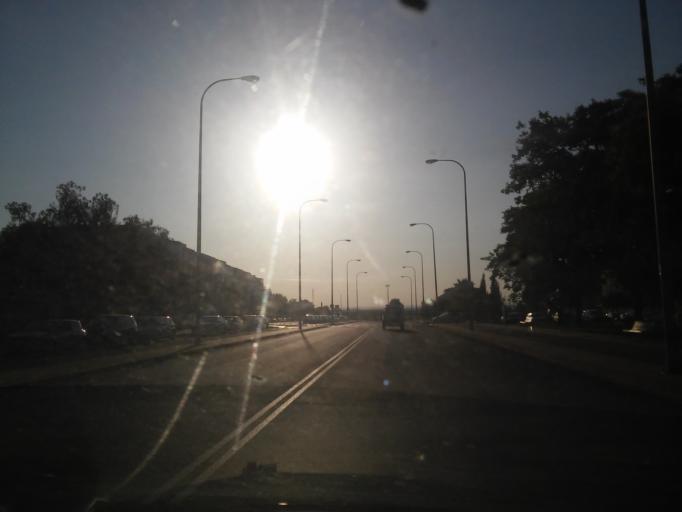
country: ES
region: Andalusia
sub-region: Provincia de Sevilla
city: La Rinconada
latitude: 37.4931
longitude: -5.9428
